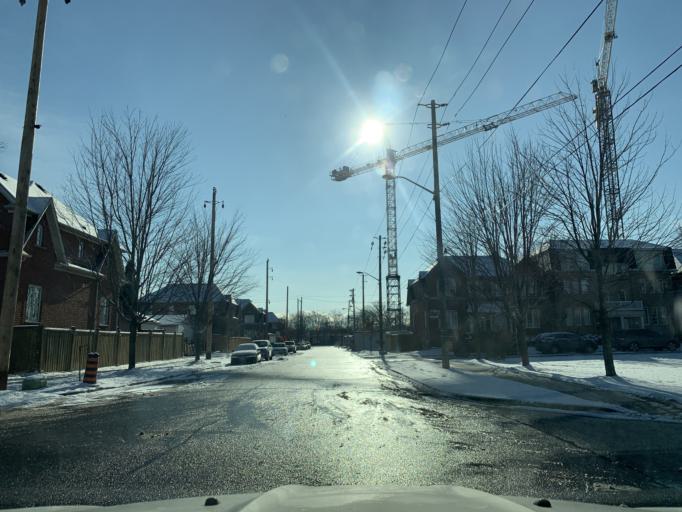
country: CA
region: Ontario
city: Toronto
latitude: 43.6717
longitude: -79.4782
